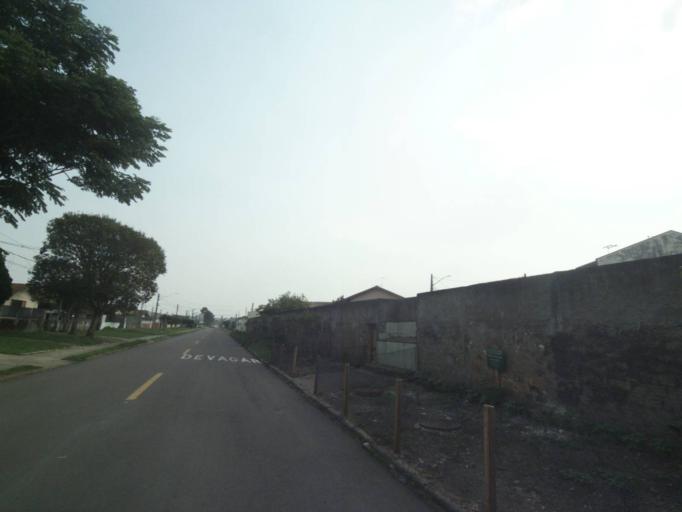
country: BR
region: Parana
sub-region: Sao Jose Dos Pinhais
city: Sao Jose dos Pinhais
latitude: -25.5268
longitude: -49.2284
